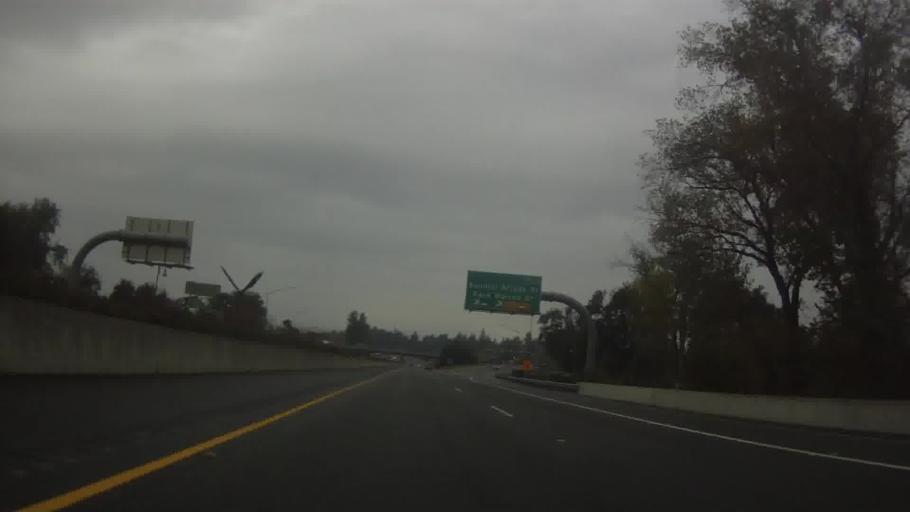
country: US
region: California
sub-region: Shasta County
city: Redding
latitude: 40.5864
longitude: -122.3742
